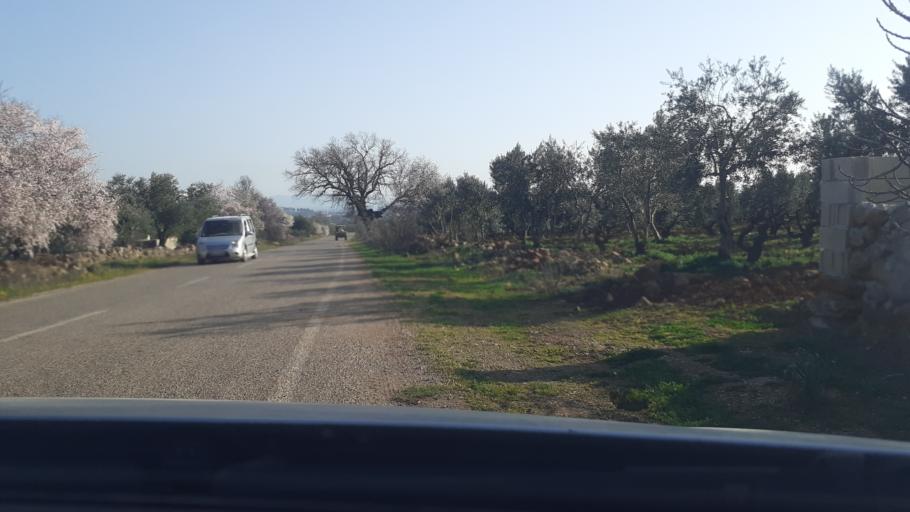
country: TR
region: Hatay
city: Aktepe
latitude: 36.7240
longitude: 36.4851
